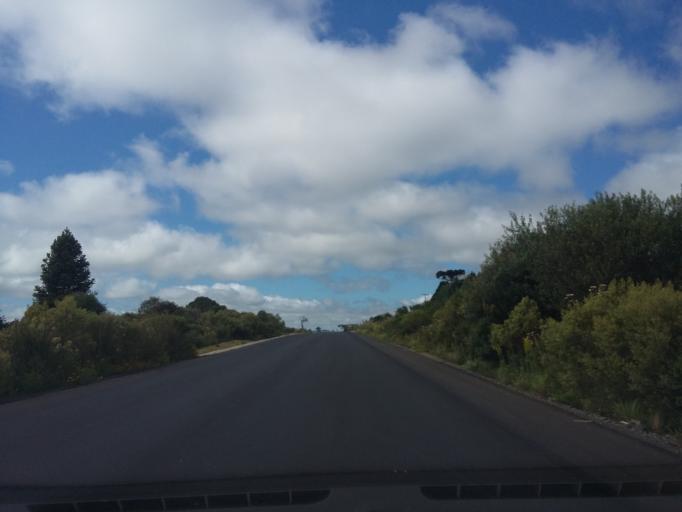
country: BR
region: Santa Catarina
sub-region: Sao Joaquim
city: Sao Joaquim
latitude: -28.0221
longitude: -50.0817
